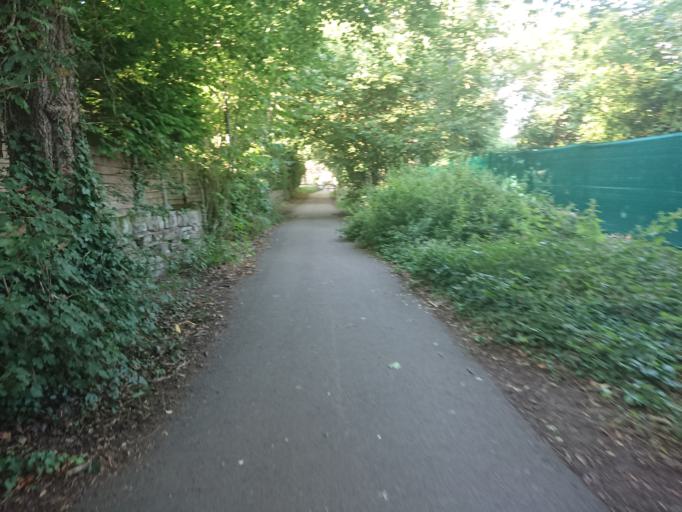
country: GB
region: England
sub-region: Sheffield
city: Sheffield
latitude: 53.3486
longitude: -1.5086
